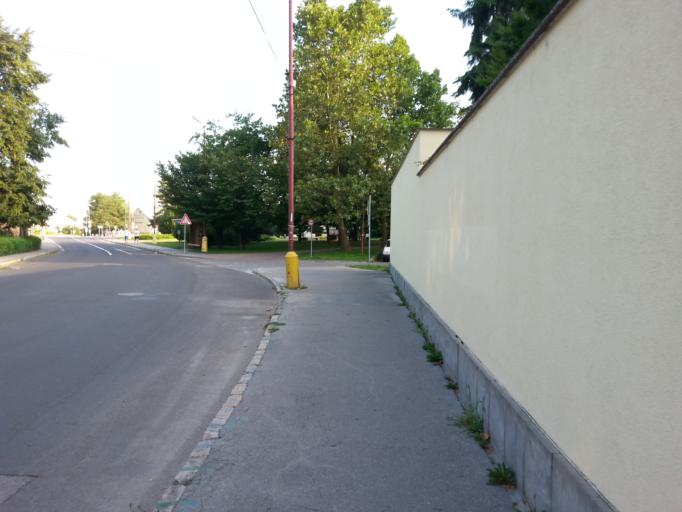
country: SK
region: Trenciansky
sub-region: Okres Nove Mesto nad Vahom
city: Nove Mesto nad Vahom
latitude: 48.7573
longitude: 17.8284
